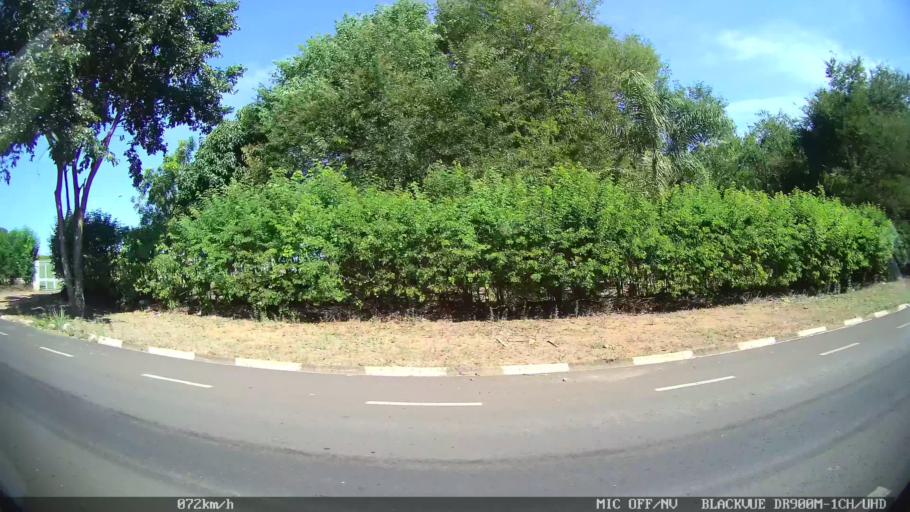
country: BR
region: Sao Paulo
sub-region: Franca
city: Franca
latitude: -20.5497
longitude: -47.4510
